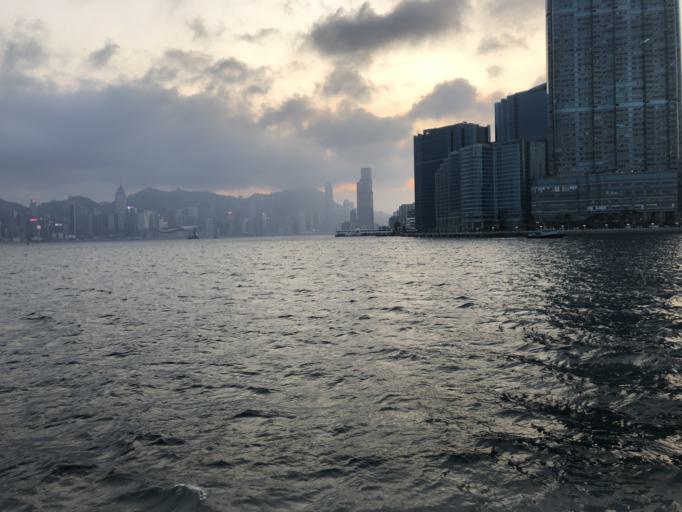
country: HK
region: Kowloon City
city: Kowloon
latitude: 22.3035
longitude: 114.1965
